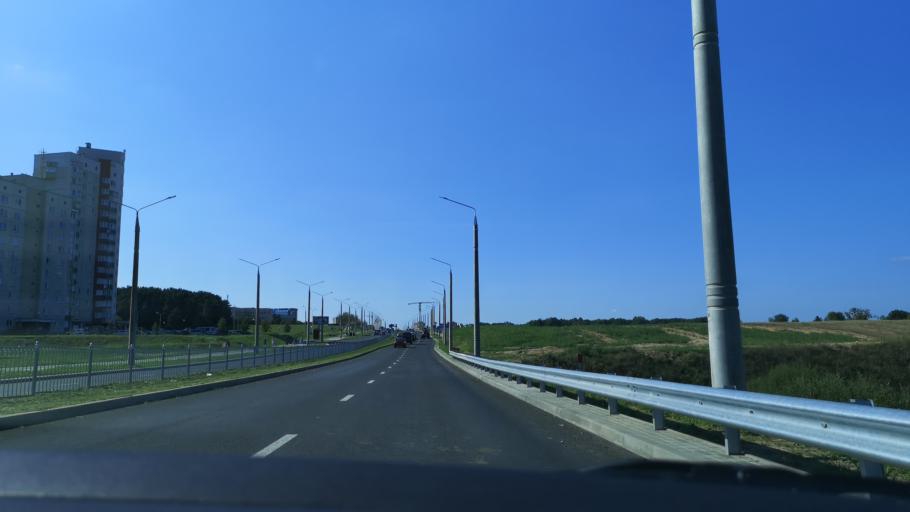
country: BY
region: Grodnenskaya
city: Hrodna
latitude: 53.6461
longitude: 23.8695
